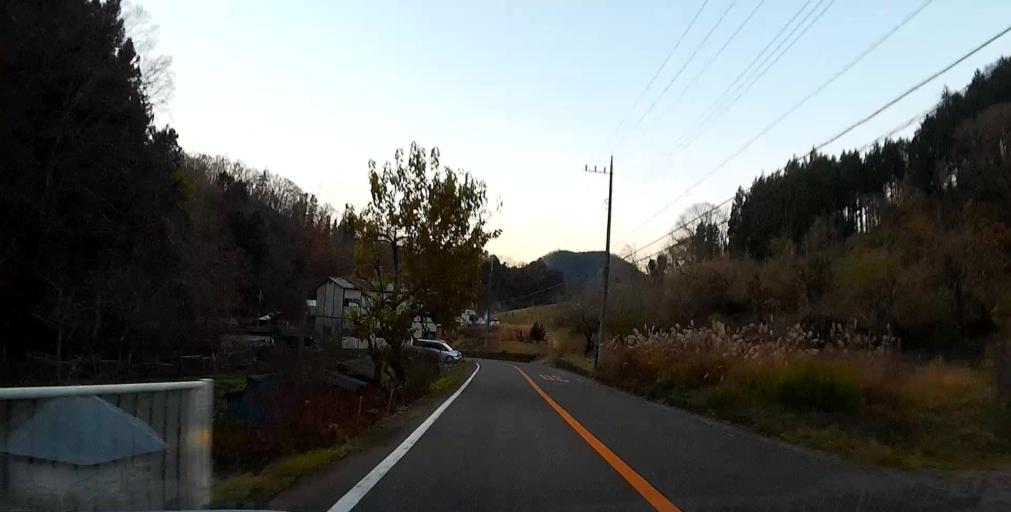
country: JP
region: Yamanashi
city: Uenohara
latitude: 35.5851
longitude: 139.1743
